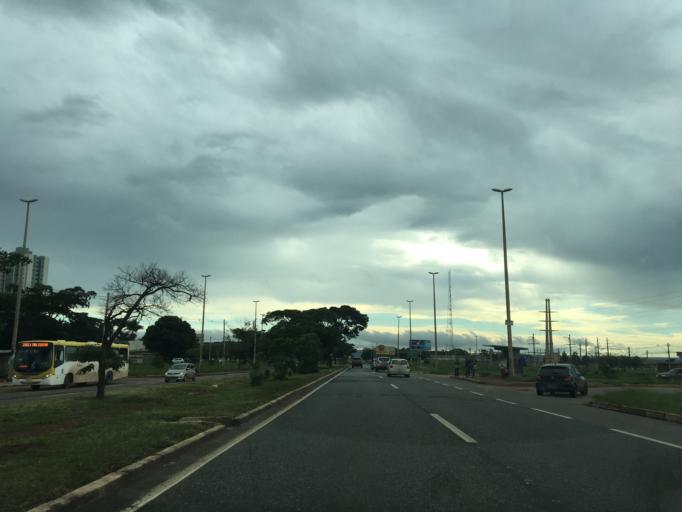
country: BR
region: Federal District
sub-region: Brasilia
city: Brasilia
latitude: -15.9966
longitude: -48.0566
